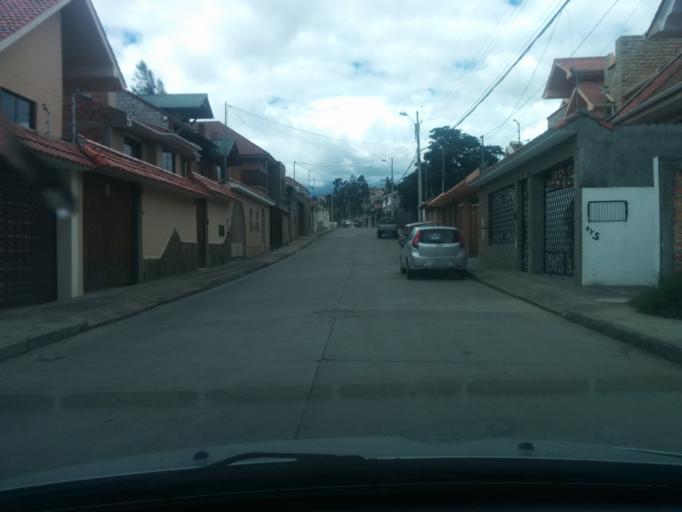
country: EC
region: Azuay
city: Cuenca
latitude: -2.8922
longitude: -78.9639
